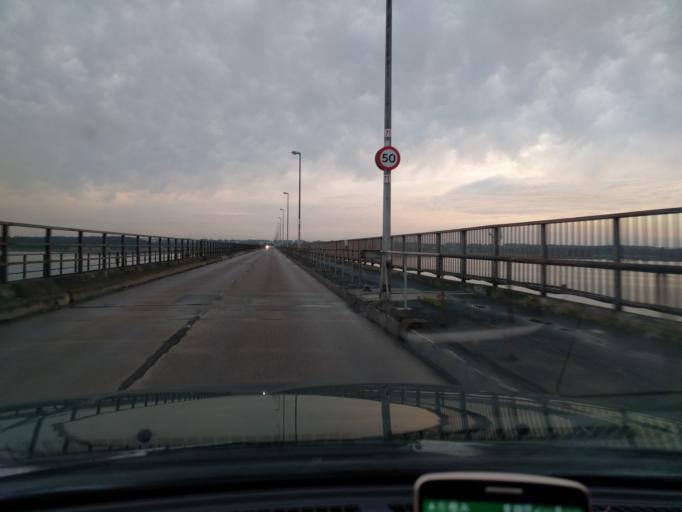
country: DK
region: Zealand
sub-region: Vordingborg Kommune
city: Vordingborg
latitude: 54.9586
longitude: 11.8761
